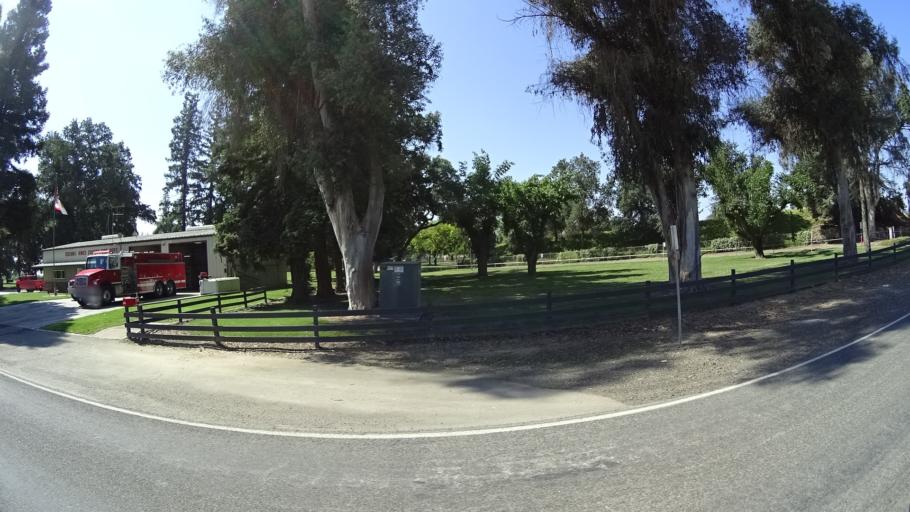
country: US
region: California
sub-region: Fresno County
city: Kingsburg
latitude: 36.4524
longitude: -119.5747
